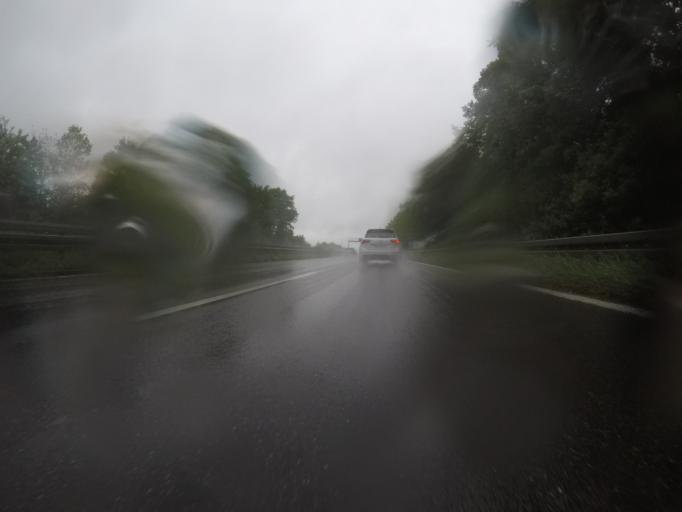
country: DE
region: Baden-Wuerttemberg
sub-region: Regierungsbezirk Stuttgart
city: Leinfelden-Echterdingen
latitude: 48.7347
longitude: 9.1655
